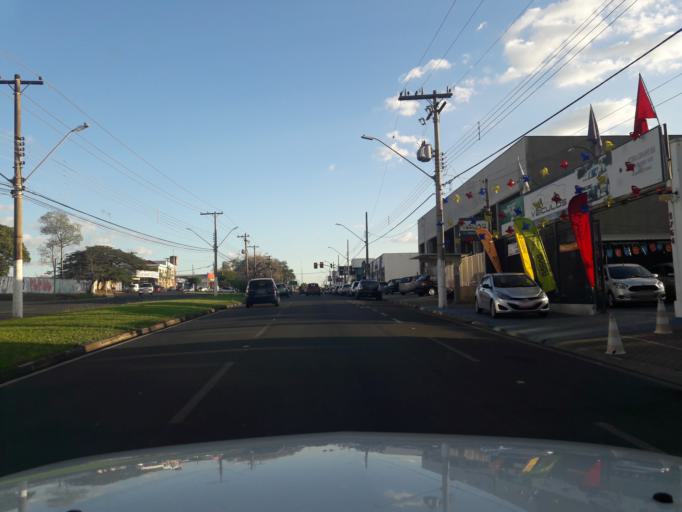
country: BR
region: Sao Paulo
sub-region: Moji-Guacu
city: Mogi-Gaucu
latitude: -22.3891
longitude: -46.9447
